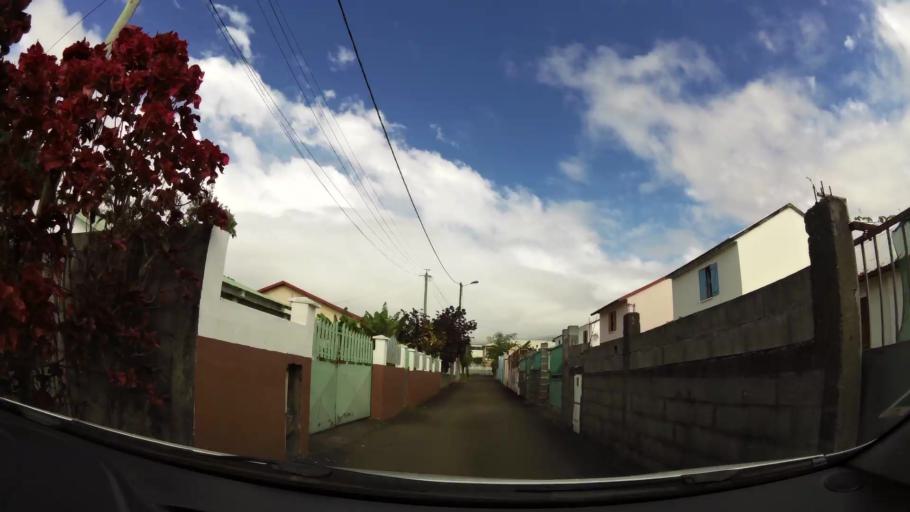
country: RE
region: Reunion
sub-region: Reunion
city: Sainte-Marie
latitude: -20.9019
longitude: 55.5690
